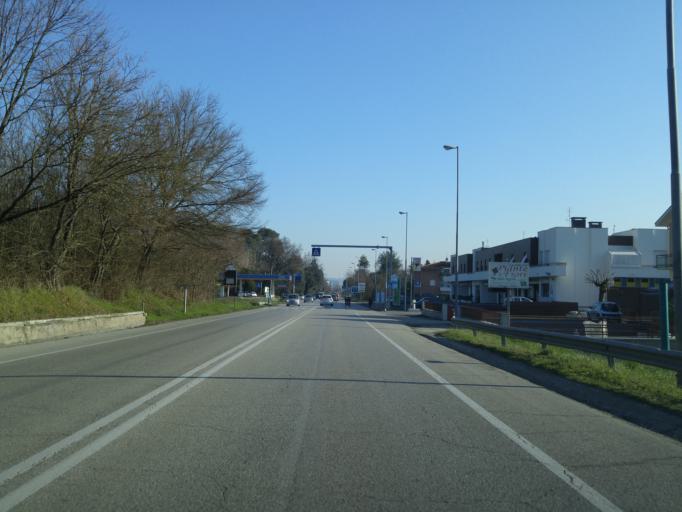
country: IT
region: The Marches
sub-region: Provincia di Pesaro e Urbino
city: Pesaro
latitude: 43.9151
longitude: 12.8656
